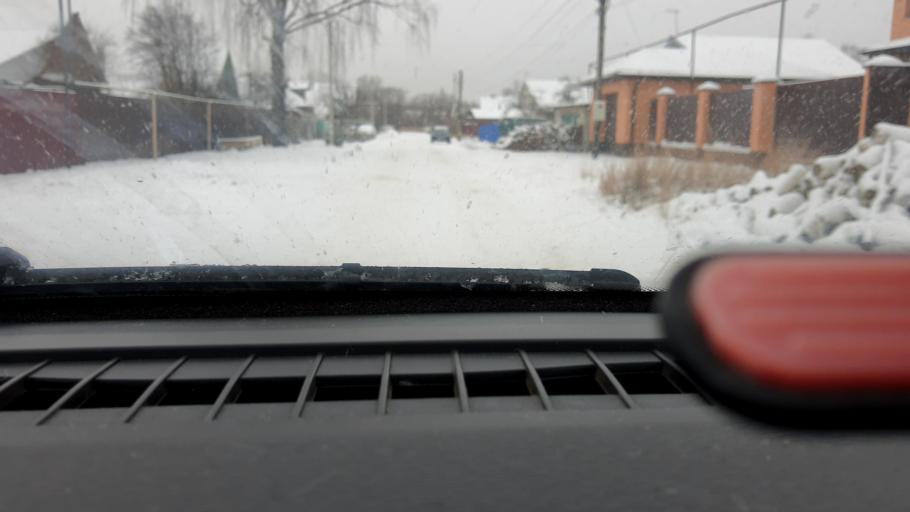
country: RU
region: Nizjnij Novgorod
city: Novaya Balakhna
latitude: 56.5180
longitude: 43.5741
